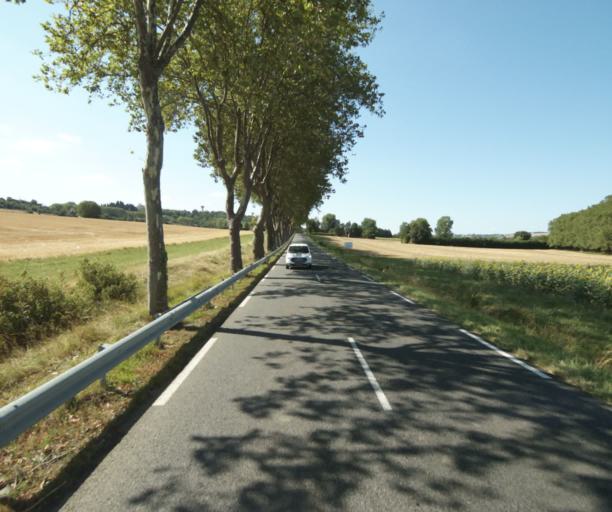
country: FR
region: Midi-Pyrenees
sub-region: Departement de la Haute-Garonne
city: Saint-Felix-Lauragais
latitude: 43.4859
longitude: 1.9098
